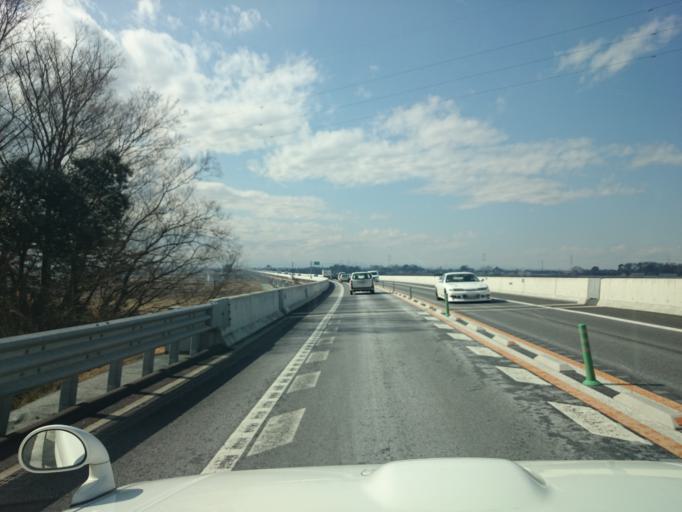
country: JP
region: Ibaraki
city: Sakai
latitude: 36.1281
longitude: 139.7910
